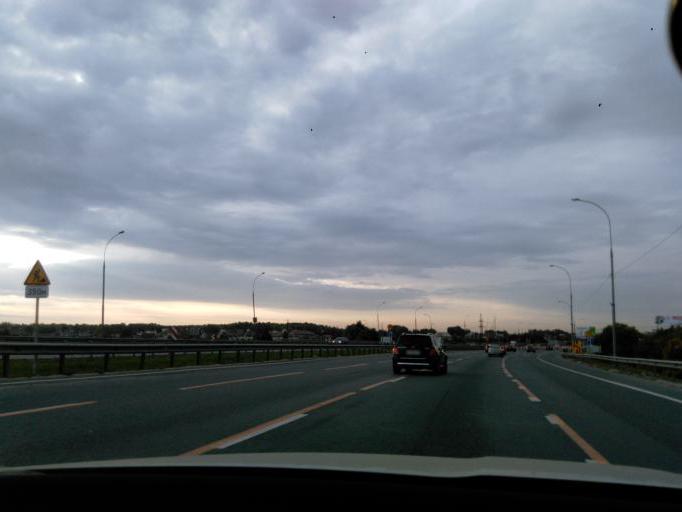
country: RU
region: Moskovskaya
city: Dolgoprudnyy
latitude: 55.9693
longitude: 37.5318
